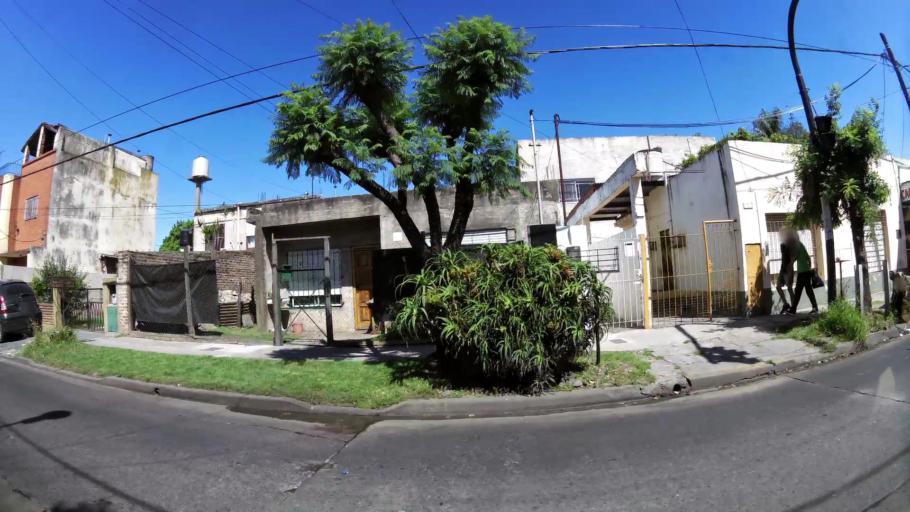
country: AR
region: Buenos Aires
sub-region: Partido de General San Martin
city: General San Martin
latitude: -34.5257
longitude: -58.5661
